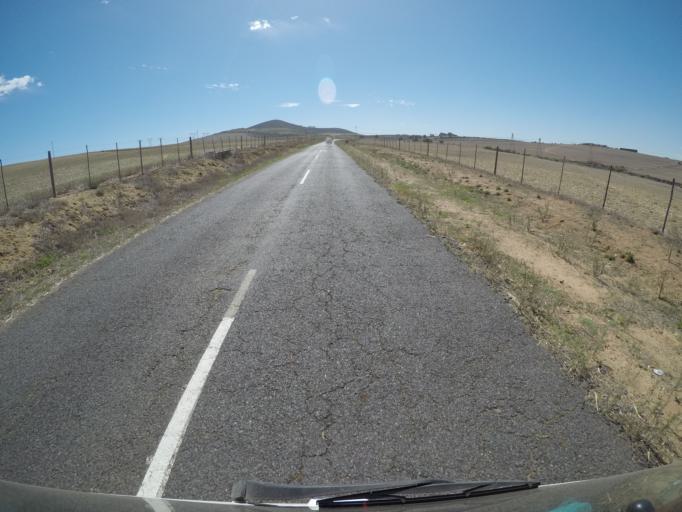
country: ZA
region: Western Cape
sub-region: City of Cape Town
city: Sunset Beach
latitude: -33.7362
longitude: 18.5659
